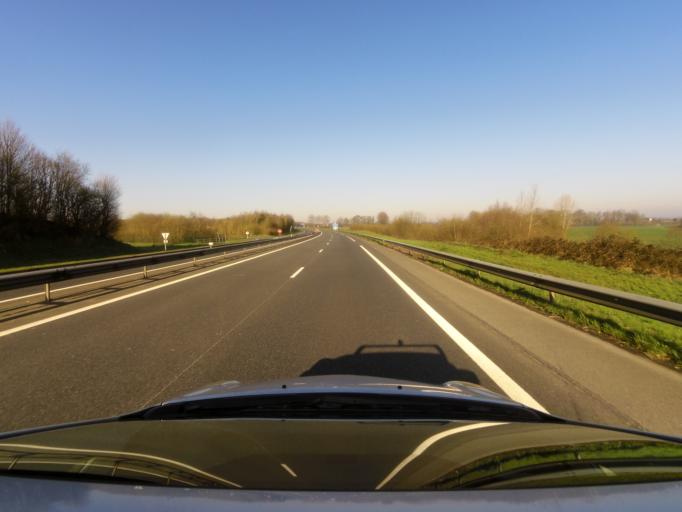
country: FR
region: Lower Normandy
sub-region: Departement du Calvados
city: Cahagnes
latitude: 49.0482
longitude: -0.7705
